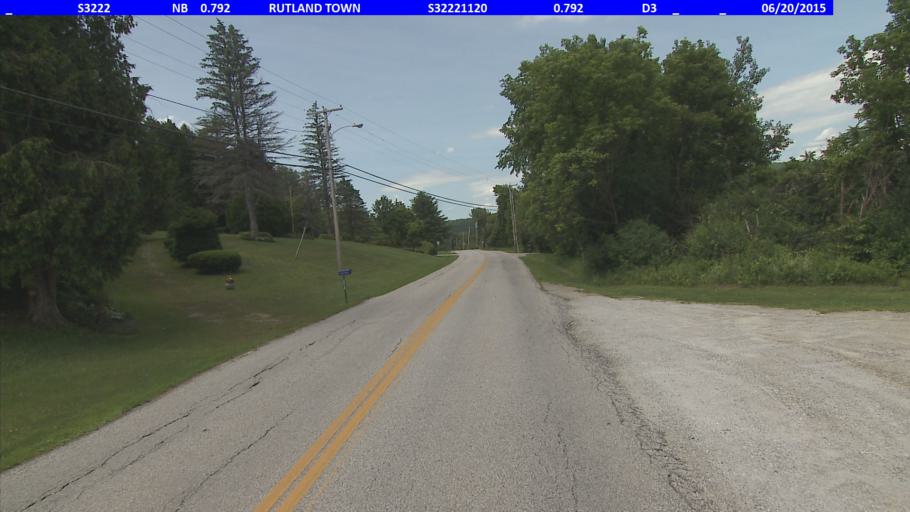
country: US
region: Vermont
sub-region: Rutland County
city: West Rutland
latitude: 43.6096
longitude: -73.0272
